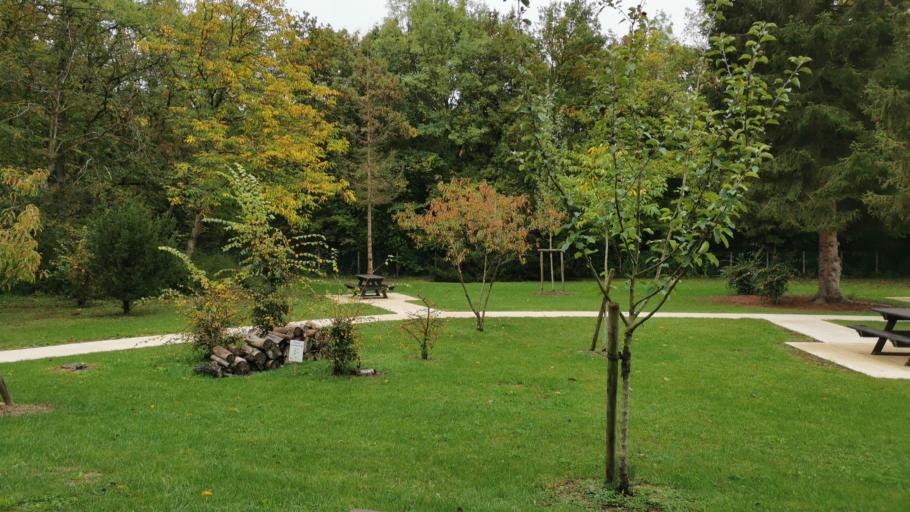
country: FR
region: Champagne-Ardenne
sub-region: Departement de l'Aube
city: Romilly-sur-Seine
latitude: 48.5446
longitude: 3.6899
